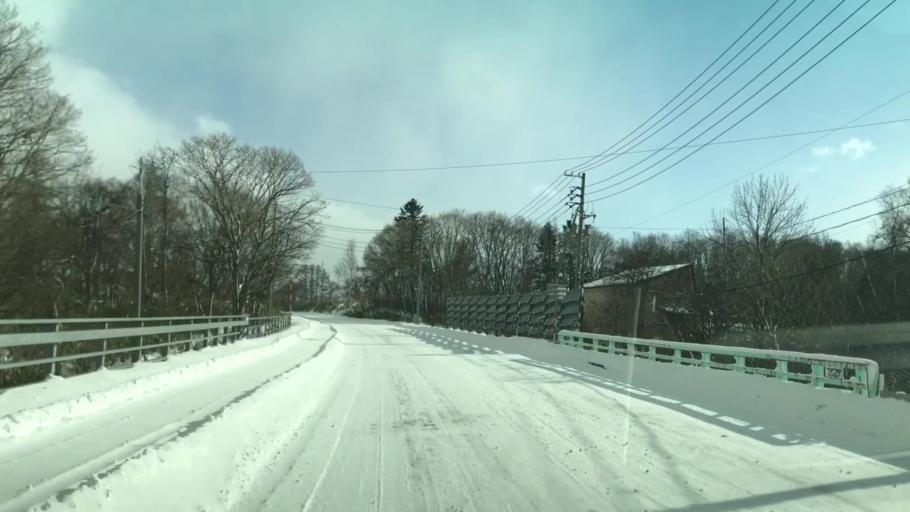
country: JP
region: Hokkaido
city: Yoichi
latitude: 43.3056
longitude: 140.5573
